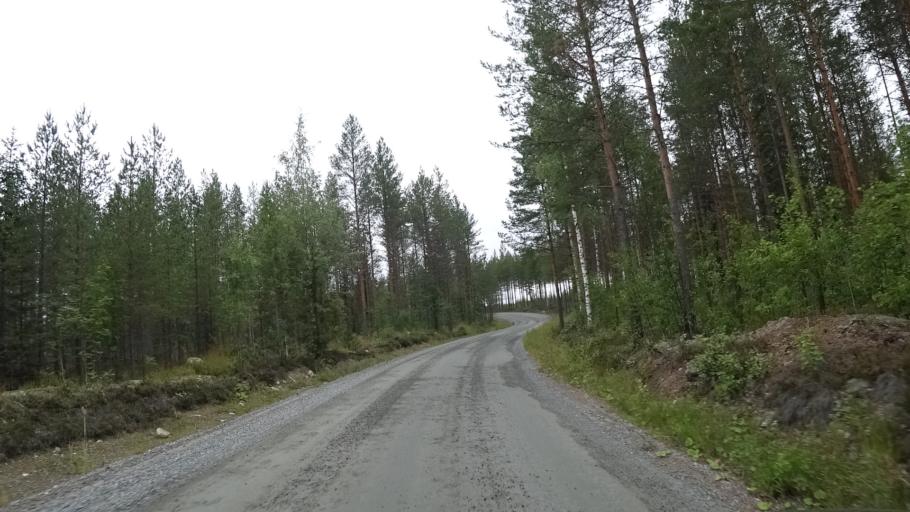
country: FI
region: North Karelia
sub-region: Pielisen Karjala
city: Lieksa
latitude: 63.3651
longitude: 30.3895
